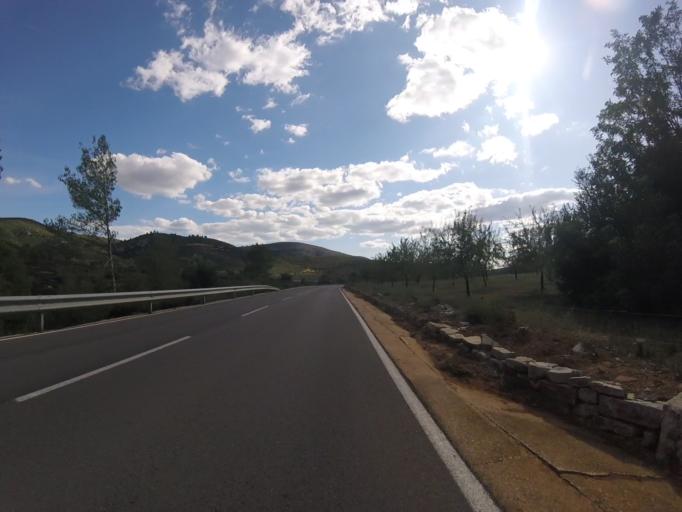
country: ES
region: Valencia
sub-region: Provincia de Castello
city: Cuevas de Vinroma
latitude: 40.3025
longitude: 0.1648
